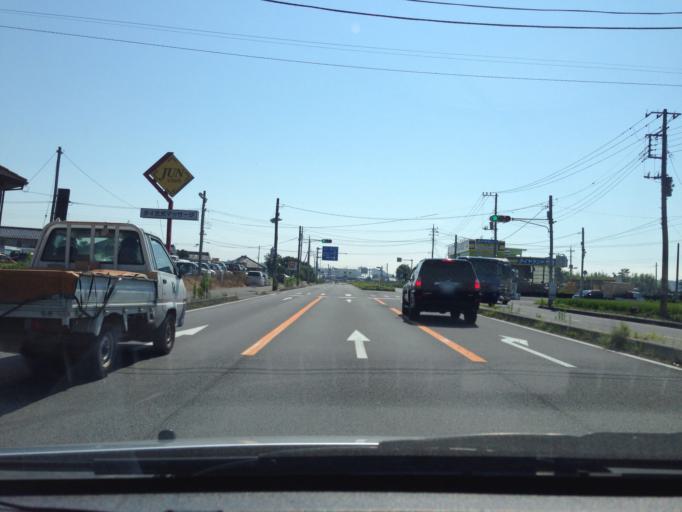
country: JP
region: Ibaraki
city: Oarai
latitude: 36.3411
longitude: 140.5682
